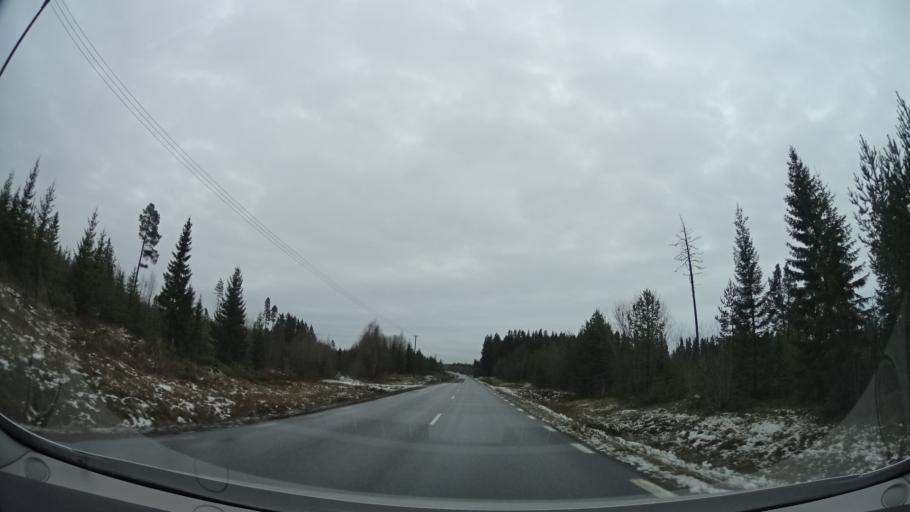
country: SE
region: Jaemtland
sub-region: Stroemsunds Kommun
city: Stroemsund
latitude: 63.9464
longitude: 15.4855
